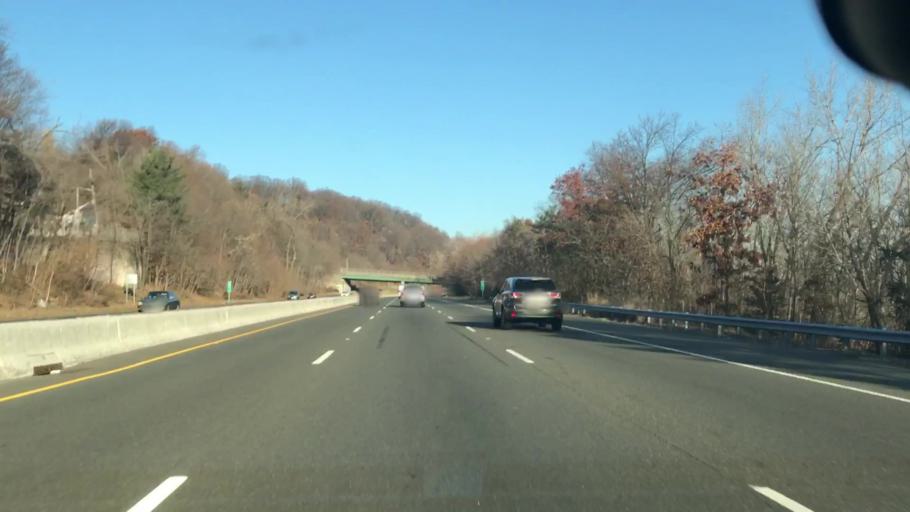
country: US
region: New Jersey
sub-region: Passaic County
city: Paterson
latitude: 40.8960
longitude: -74.1693
